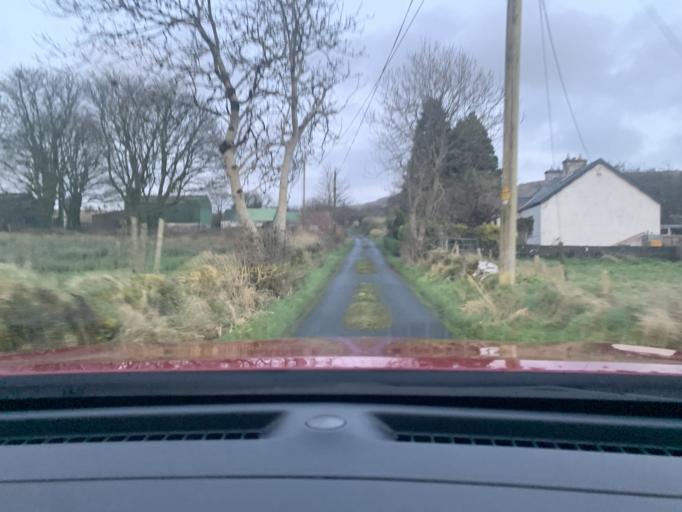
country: IE
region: Connaught
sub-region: Sligo
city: Ballymote
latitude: 54.0476
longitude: -8.4054
